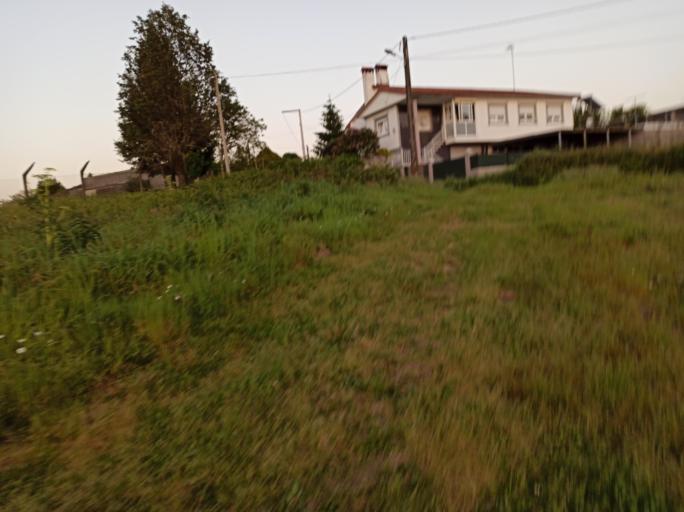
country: ES
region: Galicia
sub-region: Provincia da Coruna
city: Negreira
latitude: 42.9137
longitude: -8.7463
